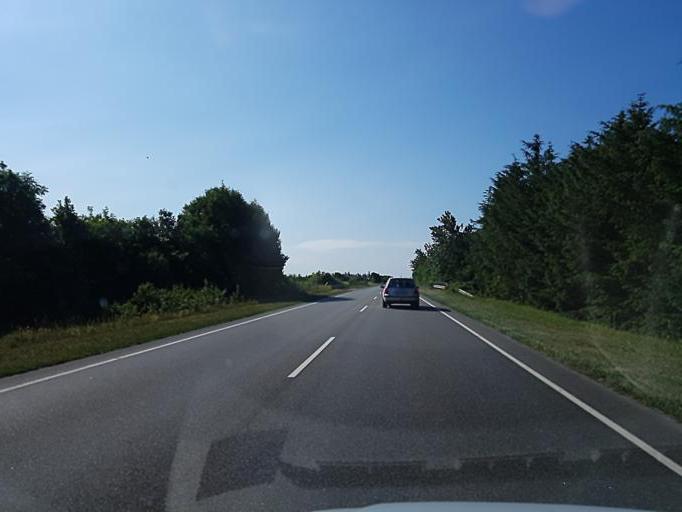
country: DK
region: South Denmark
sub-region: Varde Kommune
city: Varde
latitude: 55.6633
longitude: 8.4998
